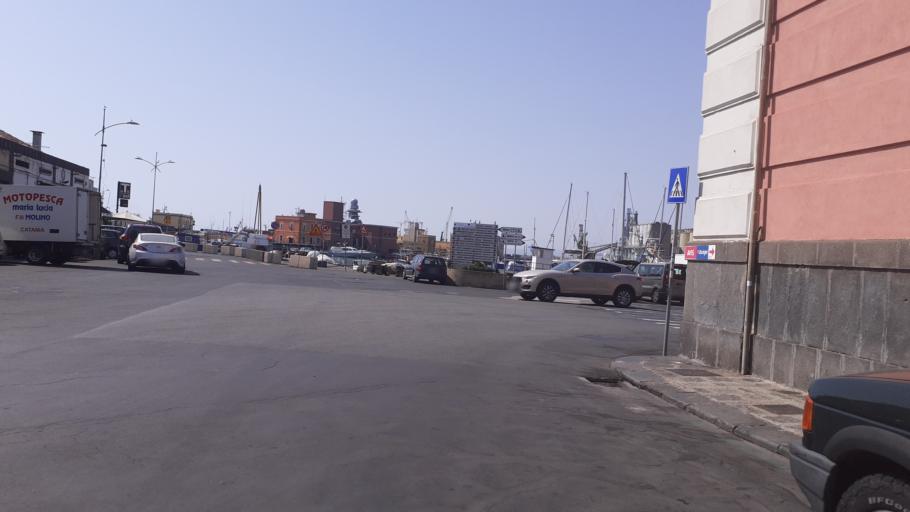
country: IT
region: Sicily
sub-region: Catania
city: Catania
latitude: 37.5008
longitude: 15.0940
